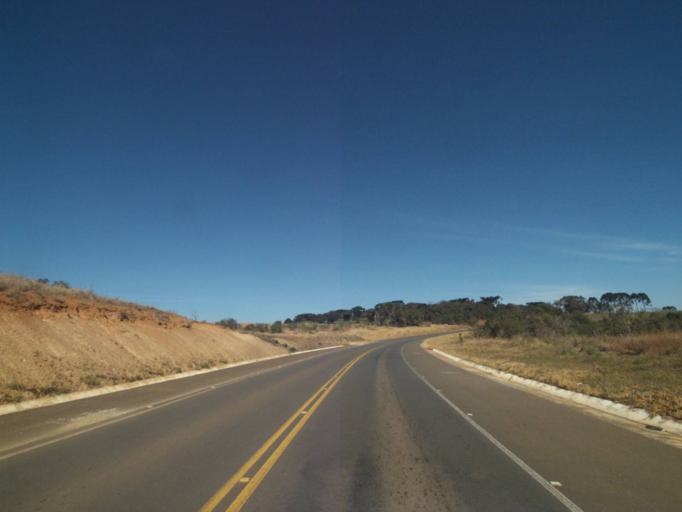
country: BR
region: Parana
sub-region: Tibagi
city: Tibagi
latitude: -24.6930
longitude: -50.4410
